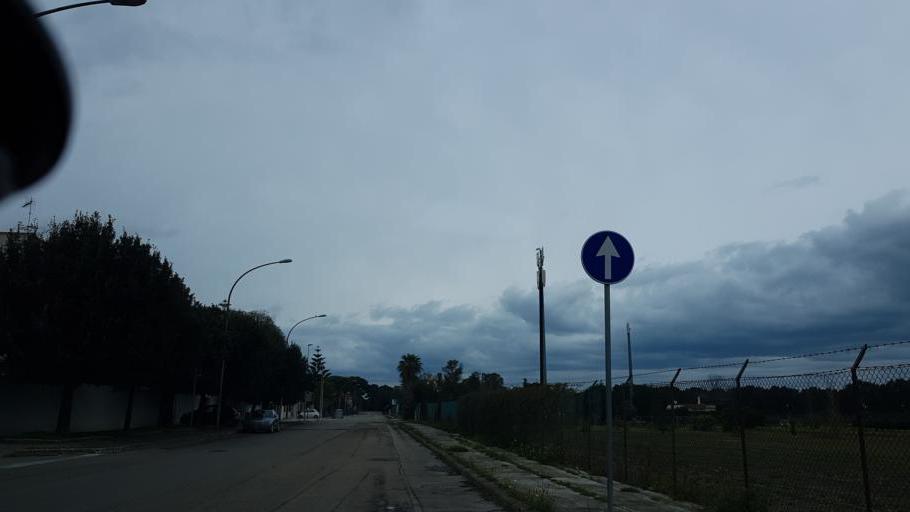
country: IT
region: Apulia
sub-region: Provincia di Brindisi
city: La Rosa
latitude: 40.6062
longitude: 17.9539
